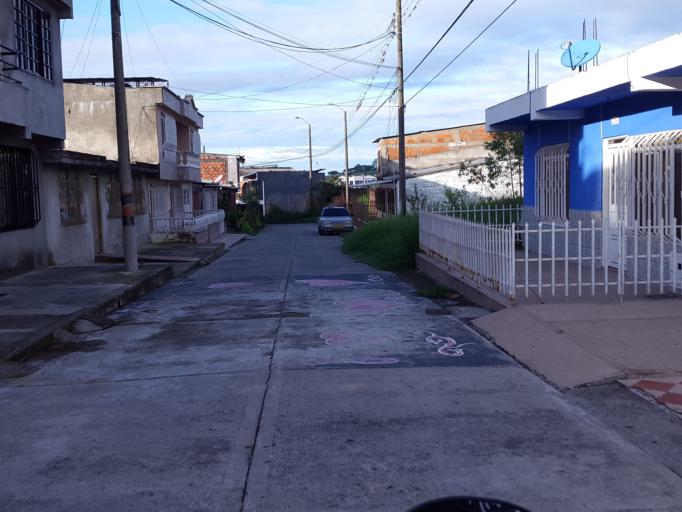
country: CO
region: Quindio
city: Montenegro
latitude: 4.5635
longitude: -75.7508
